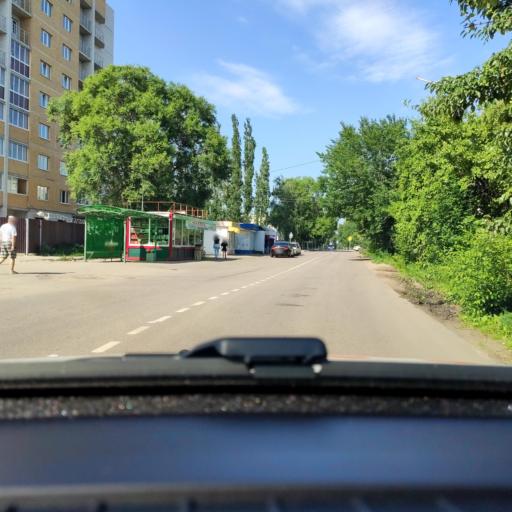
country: RU
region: Voronezj
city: Semiluki
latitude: 51.6923
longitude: 39.0130
